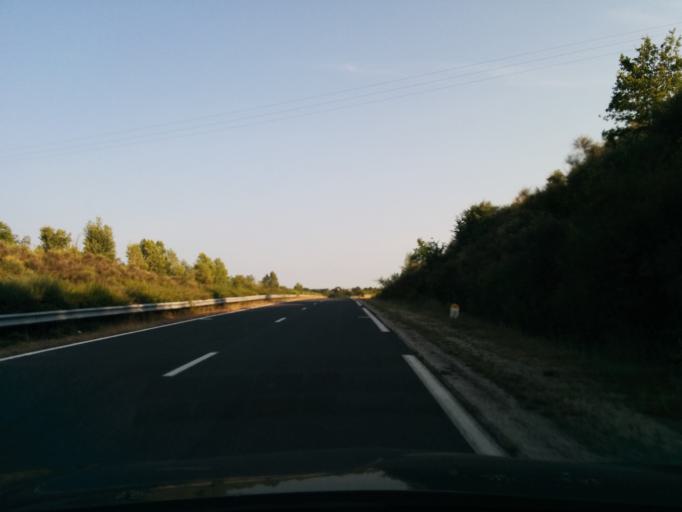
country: FR
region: Midi-Pyrenees
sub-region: Departement du Lot
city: Souillac
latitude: 44.8192
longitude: 1.4777
